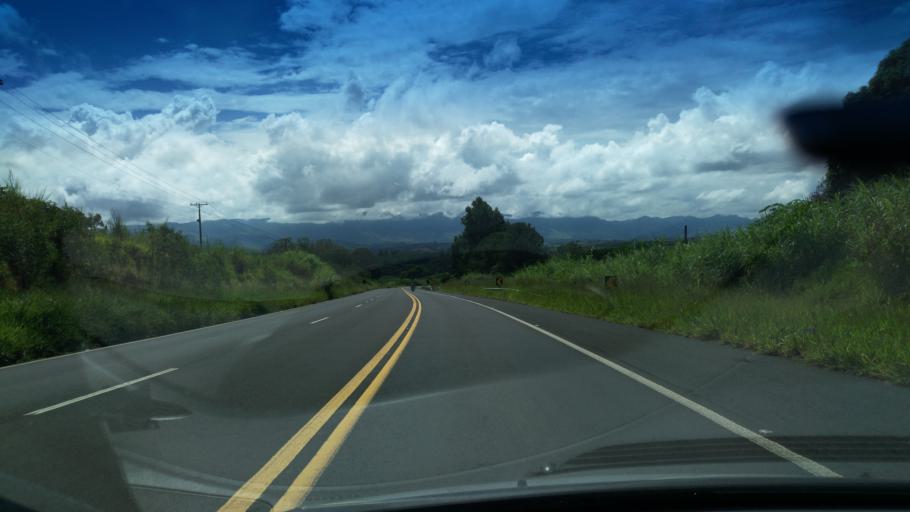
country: BR
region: Sao Paulo
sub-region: Santo Antonio Do Jardim
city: Espirito Santo do Pinhal
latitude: -22.1367
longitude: -46.7024
